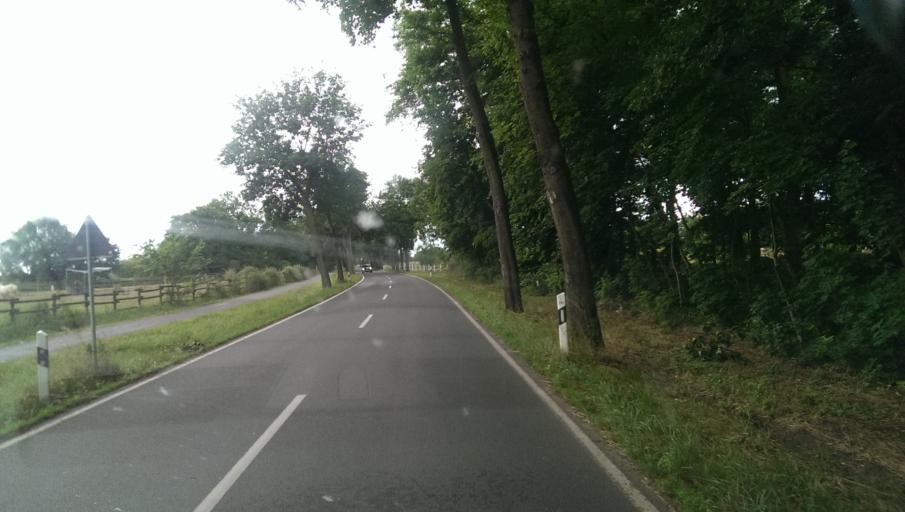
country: DE
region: Brandenburg
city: Stahnsdorf
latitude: 52.3385
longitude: 13.1892
